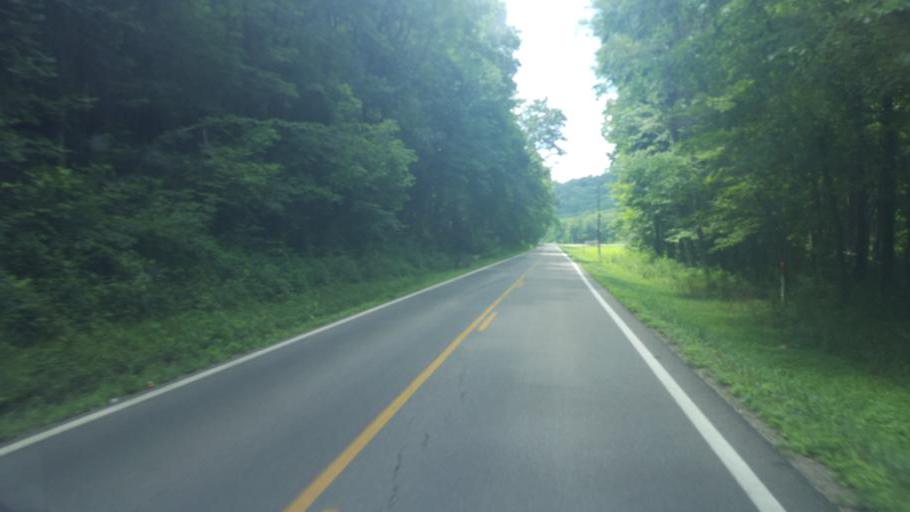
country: US
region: Ohio
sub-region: Ross County
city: Kingston
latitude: 39.3771
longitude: -82.7288
